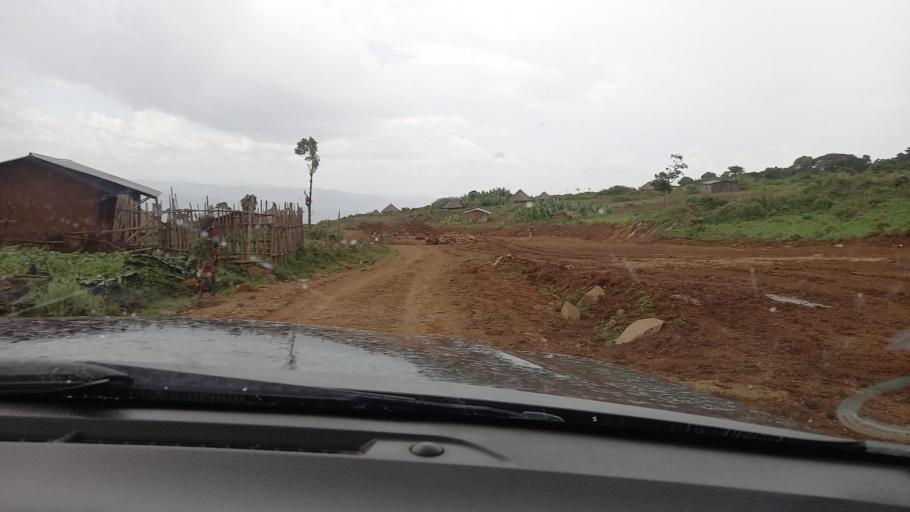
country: ET
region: Southern Nations, Nationalities, and People's Region
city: Mizan Teferi
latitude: 6.1644
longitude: 35.7259
